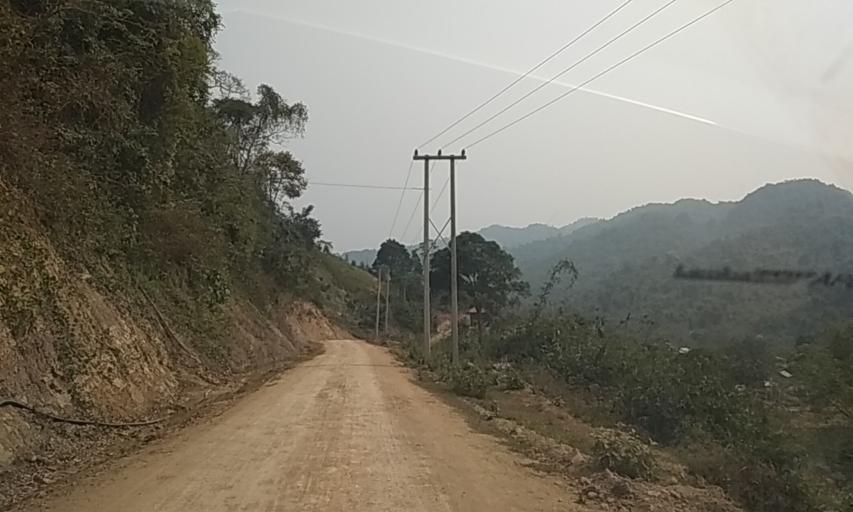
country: VN
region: Huyen Dien Bien
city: Dien Bien Phu
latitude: 21.4313
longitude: 102.7639
